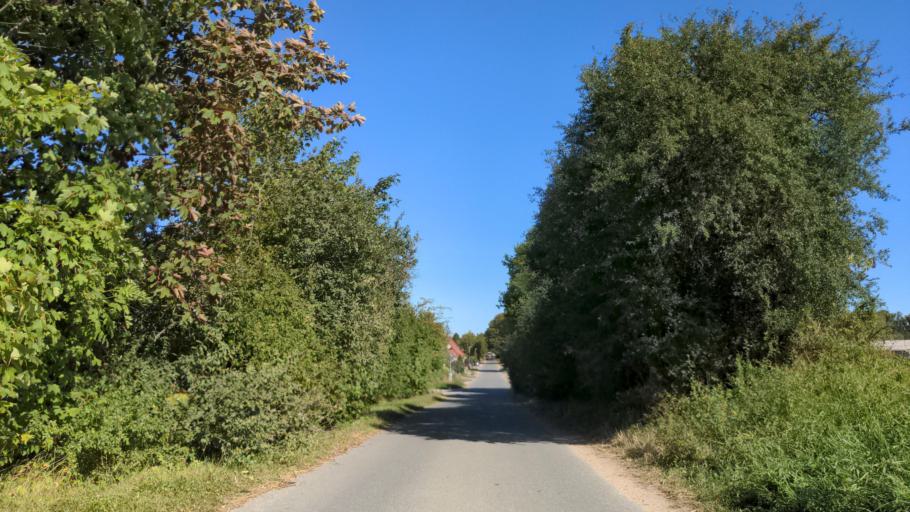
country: DE
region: Mecklenburg-Vorpommern
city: Ostseebad Boltenhagen
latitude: 53.9423
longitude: 11.2241
